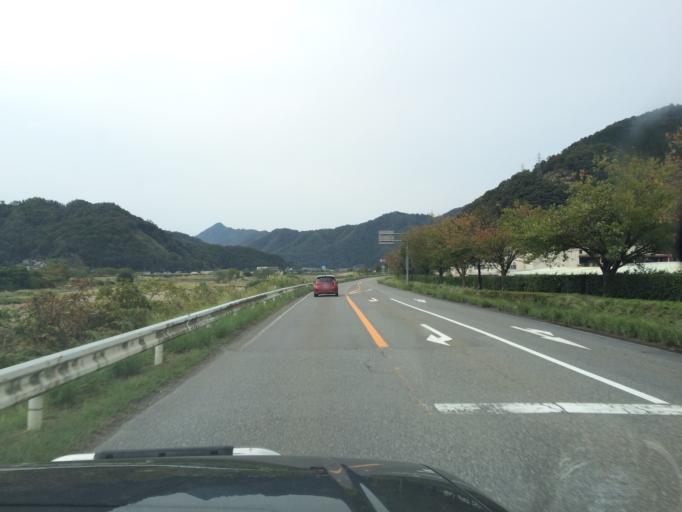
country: JP
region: Hyogo
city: Toyooka
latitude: 35.3925
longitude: 134.7951
